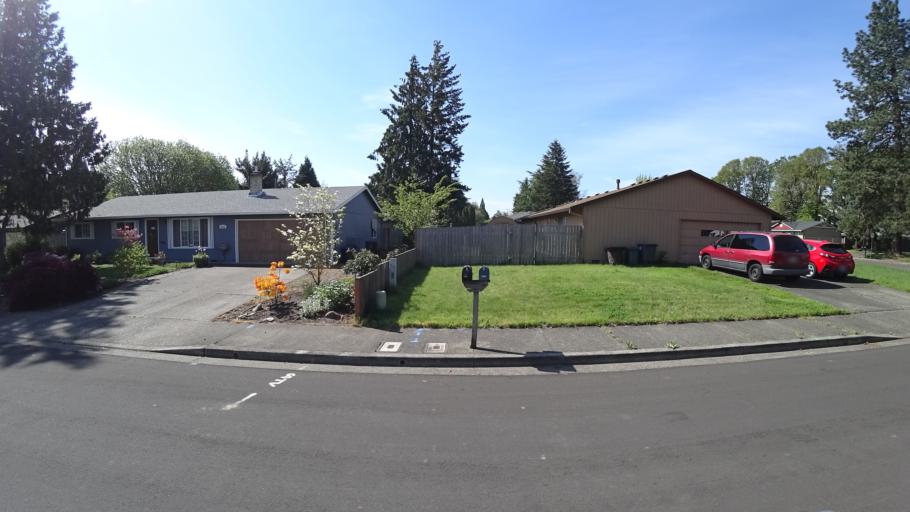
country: US
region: Oregon
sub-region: Washington County
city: Hillsboro
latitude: 45.5261
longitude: -122.9438
